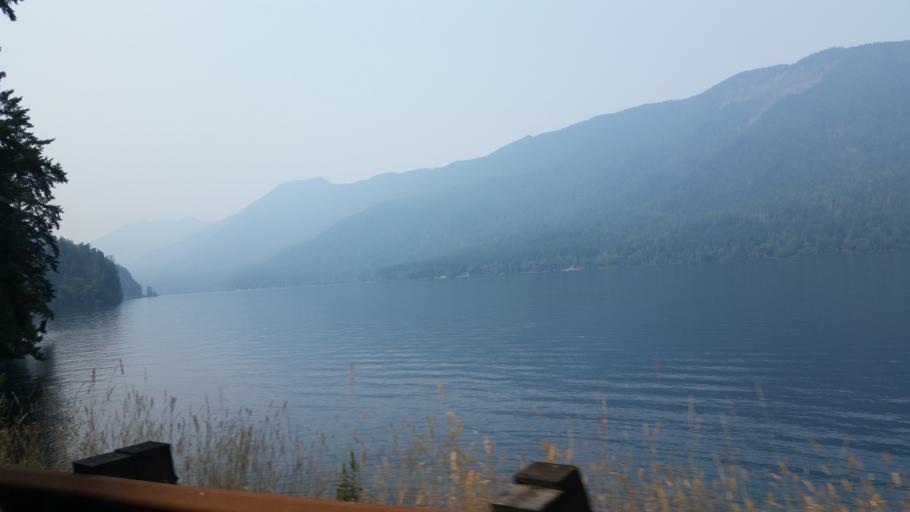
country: CA
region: British Columbia
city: Sooke
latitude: 48.0490
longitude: -123.8545
